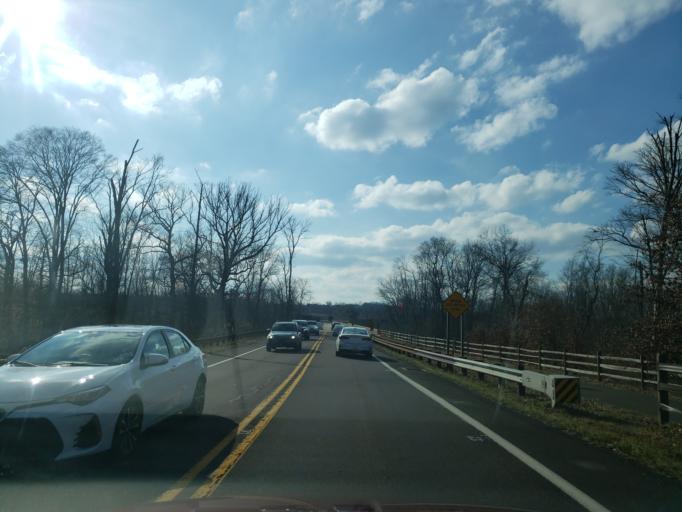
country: US
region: Pennsylvania
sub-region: Bucks County
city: New Britain
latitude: 40.2834
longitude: -75.1722
